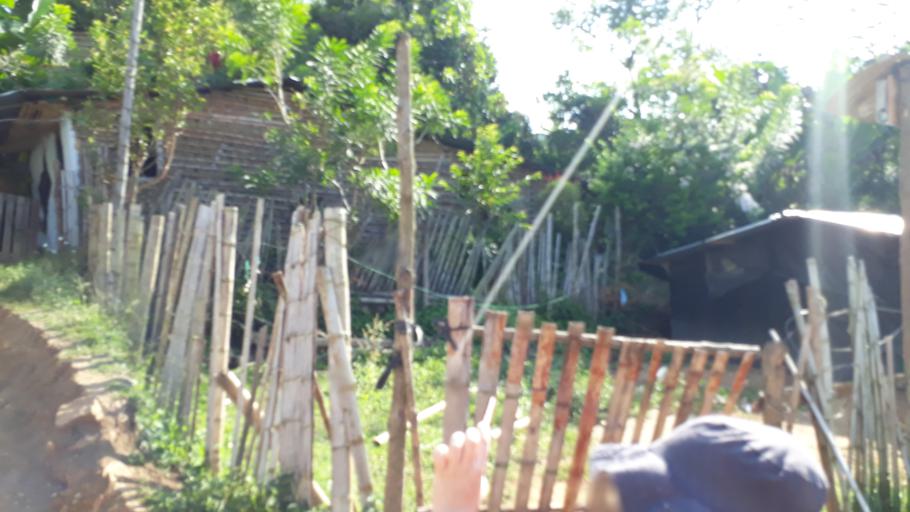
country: CO
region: Cauca
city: Buenos Aires
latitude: 3.1266
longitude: -76.6236
